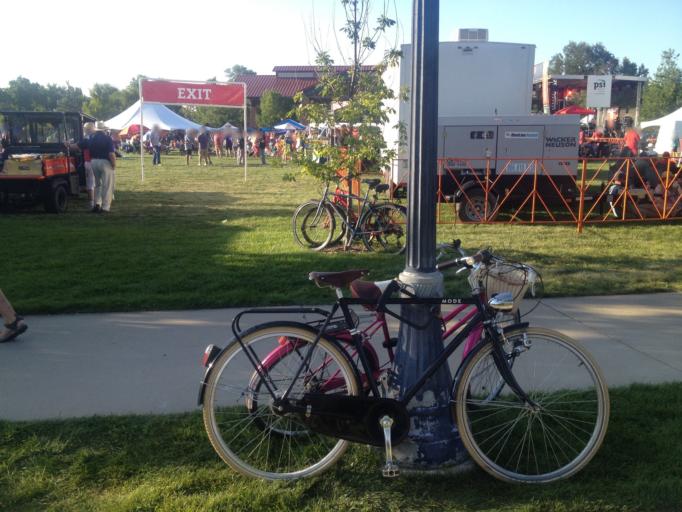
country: US
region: Colorado
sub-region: Boulder County
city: Longmont
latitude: 40.1713
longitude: -105.1057
